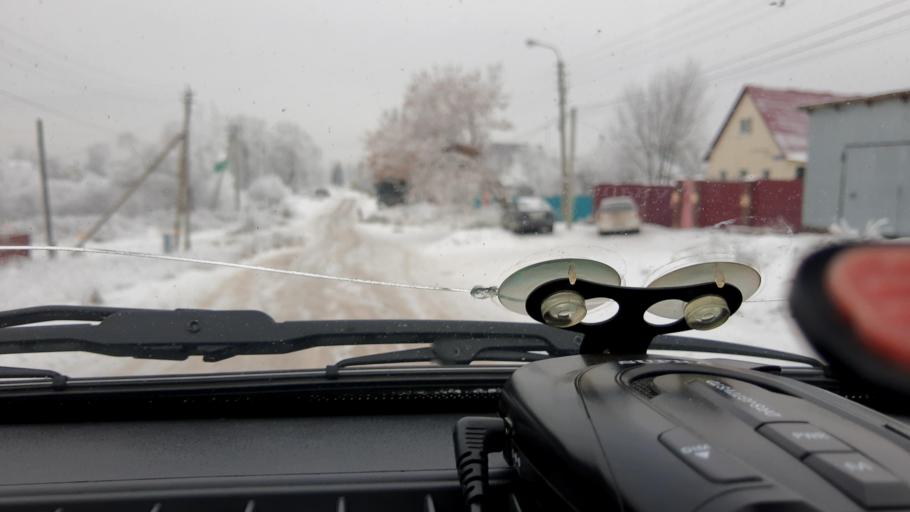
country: RU
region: Bashkortostan
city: Iglino
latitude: 54.7826
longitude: 56.2317
